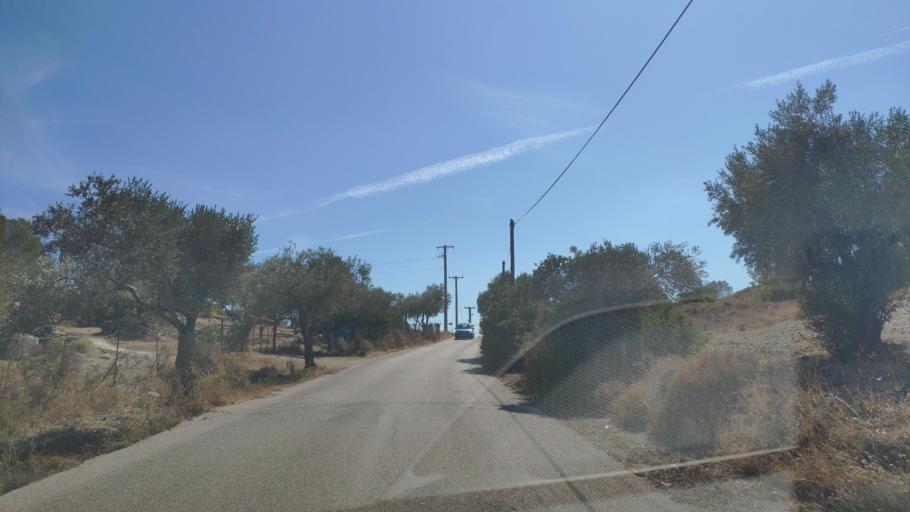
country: GR
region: Attica
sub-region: Nomarchia Anatolikis Attikis
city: Kouvaras
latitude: 37.8322
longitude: 23.9914
